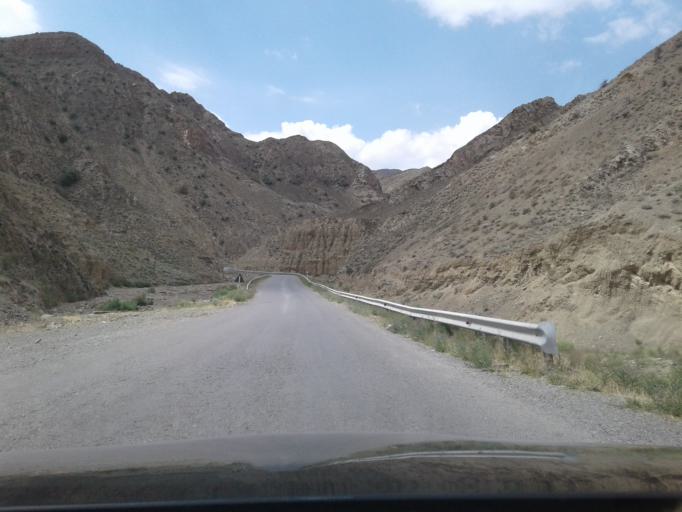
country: TM
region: Ahal
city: Baharly
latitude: 38.5046
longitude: 57.0506
